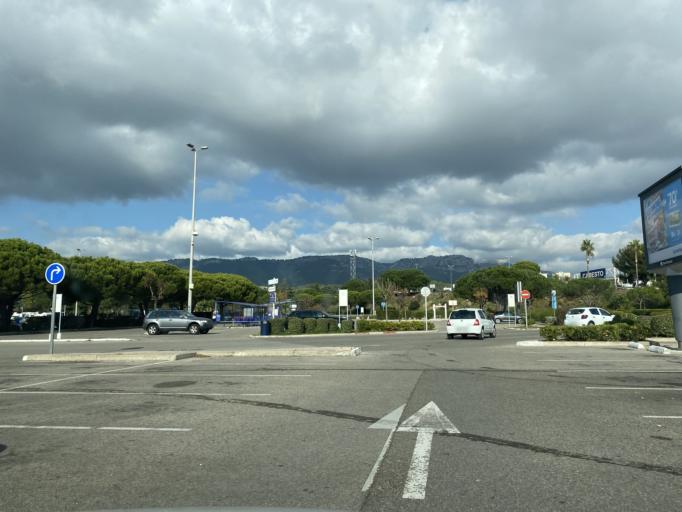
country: FR
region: Provence-Alpes-Cote d'Azur
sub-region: Departement du Var
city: La Seyne-sur-Mer
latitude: 43.1234
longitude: 5.8778
